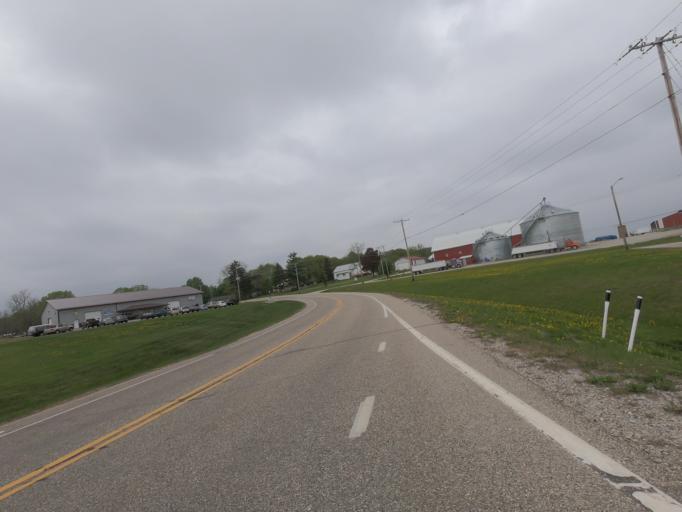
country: US
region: Wisconsin
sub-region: Jefferson County
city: Jefferson
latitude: 43.0300
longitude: -88.8078
